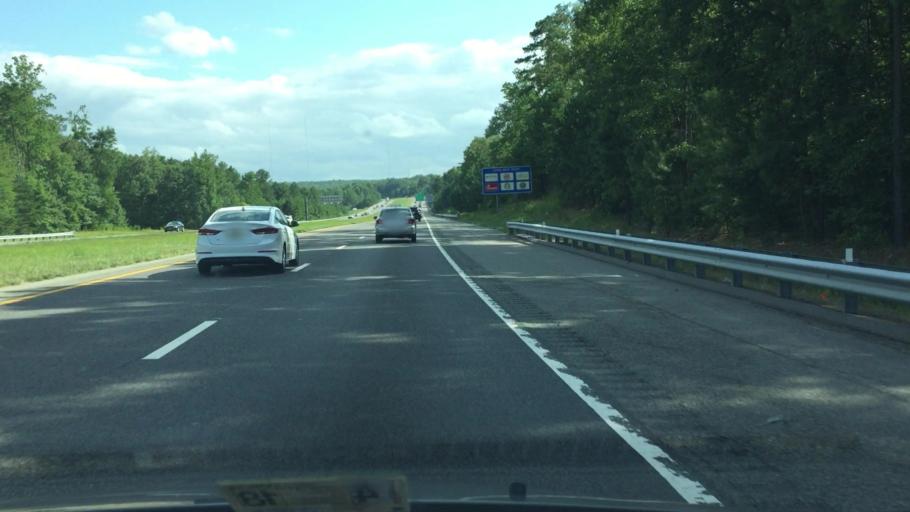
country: US
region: Virginia
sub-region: Chesterfield County
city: Brandermill
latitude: 37.5436
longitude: -77.6944
